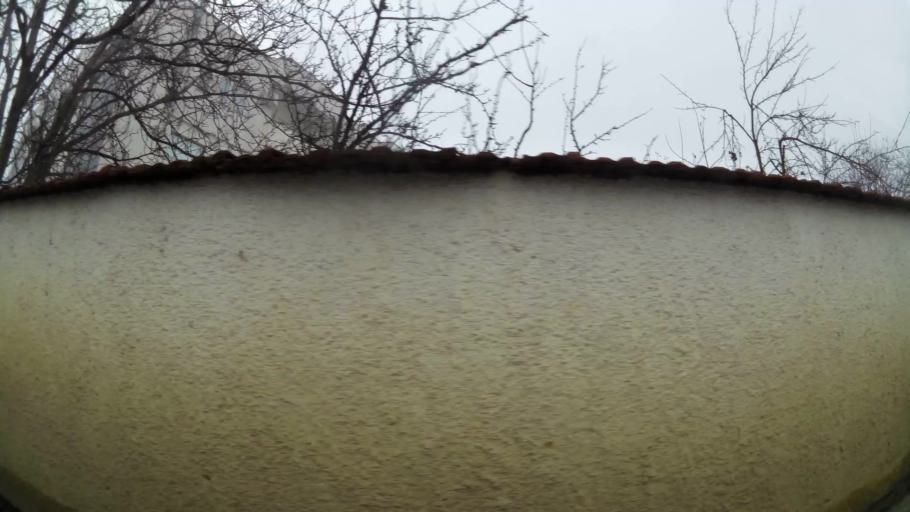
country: XK
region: Pristina
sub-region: Komuna e Prishtines
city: Pristina
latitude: 42.6420
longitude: 21.1449
